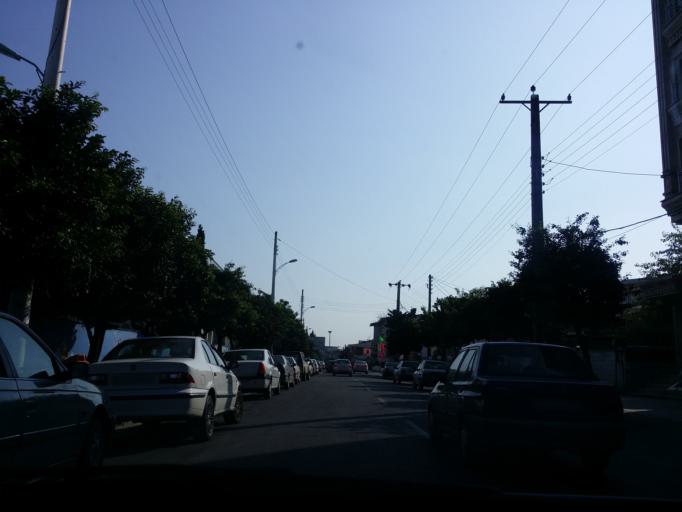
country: IR
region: Mazandaran
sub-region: Nowshahr
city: Nowshahr
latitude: 36.6520
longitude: 51.4982
